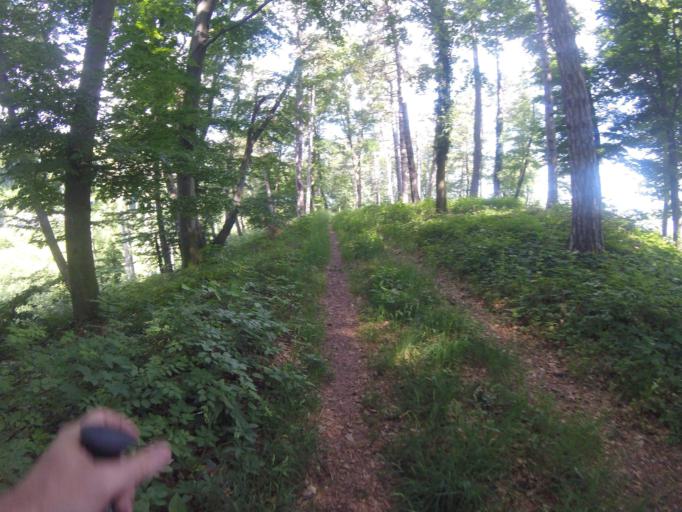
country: HU
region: Fejer
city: Bakonycsernye
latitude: 47.2702
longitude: 18.0418
